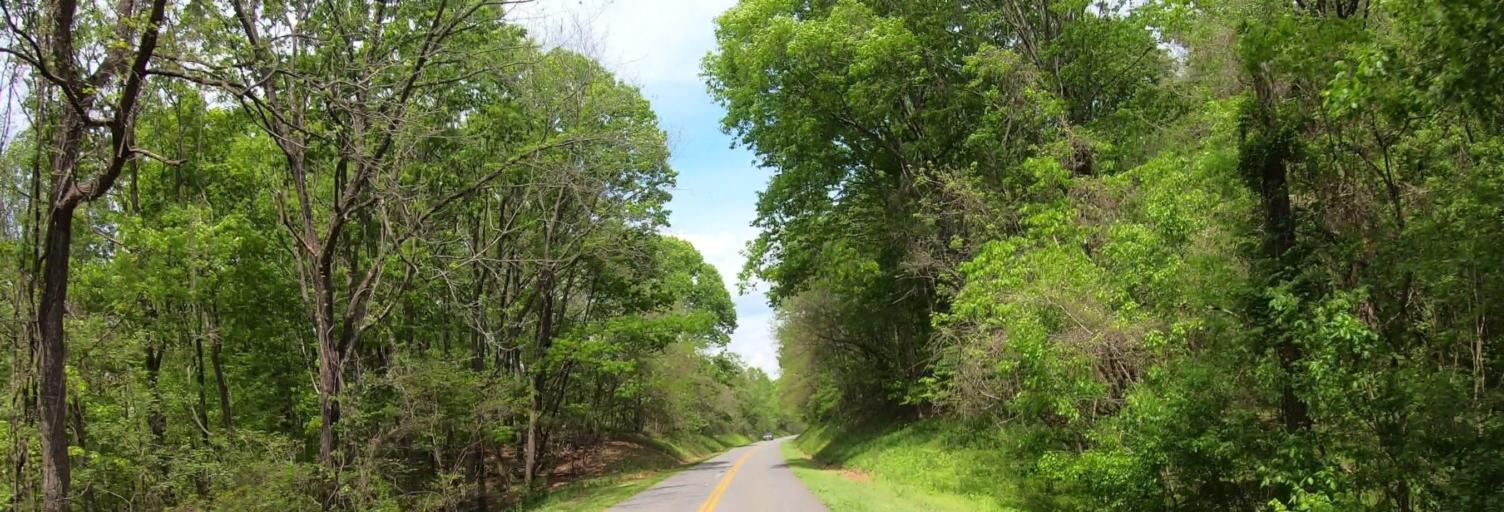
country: US
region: Virginia
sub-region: Roanoke County
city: Vinton
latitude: 37.3048
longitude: -79.8682
